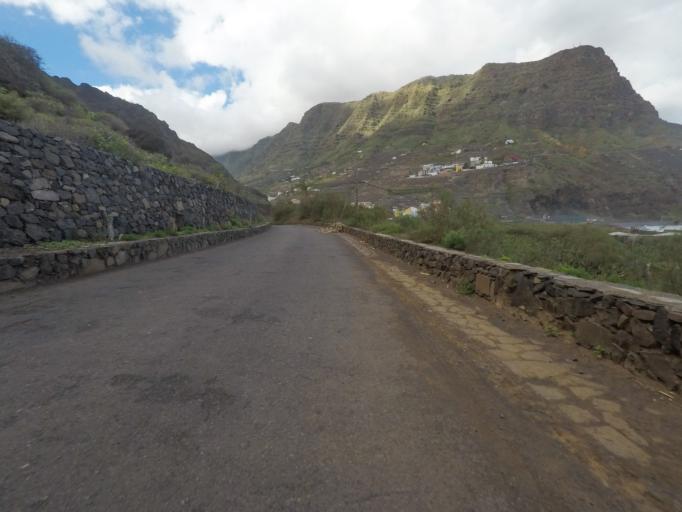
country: ES
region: Canary Islands
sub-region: Provincia de Santa Cruz de Tenerife
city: Hermigua
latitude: 28.1771
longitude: -17.1782
